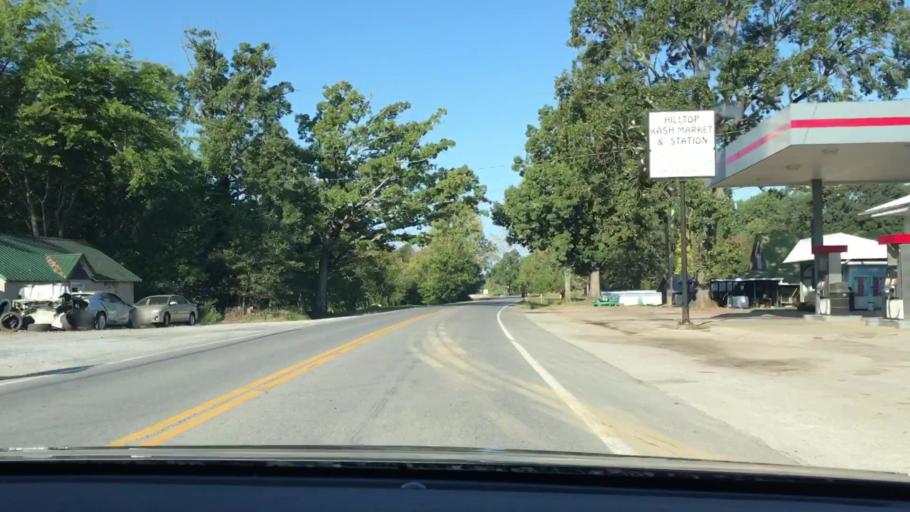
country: US
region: Kentucky
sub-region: Trigg County
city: Cadiz
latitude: 36.8109
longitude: -87.8904
